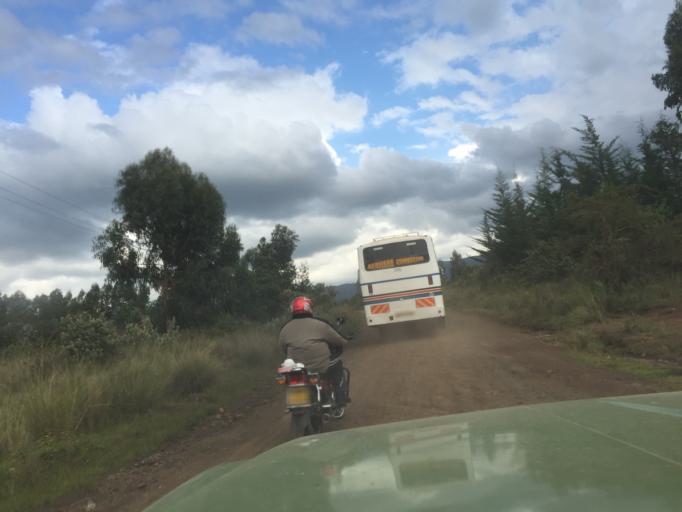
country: KE
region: Nyandarua
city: Ol Kalou
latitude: -0.4157
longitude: 36.4539
